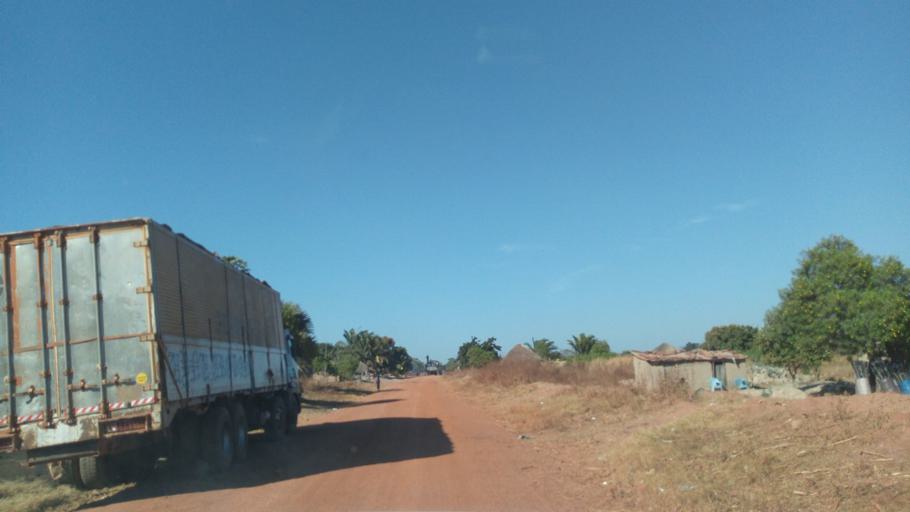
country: ZM
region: Luapula
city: Mwense
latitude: -10.6268
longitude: 28.4114
